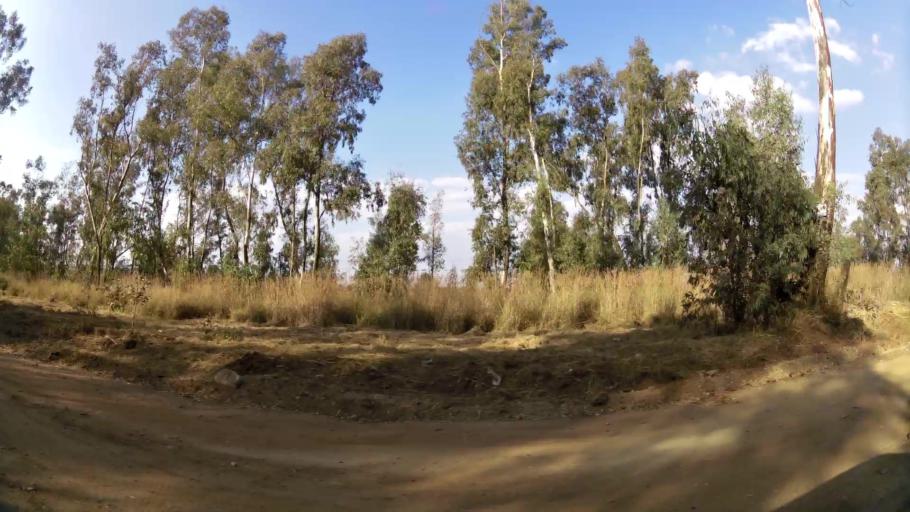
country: ZA
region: Gauteng
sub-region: Ekurhuleni Metropolitan Municipality
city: Tembisa
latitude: -25.9362
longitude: 28.2328
